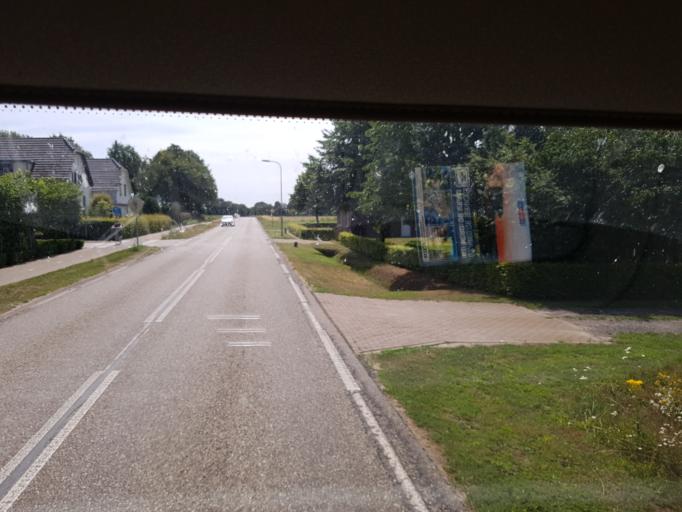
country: NL
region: Limburg
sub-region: Gemeente Leudal
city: Kelpen-Oler
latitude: 51.2061
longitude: 5.8048
